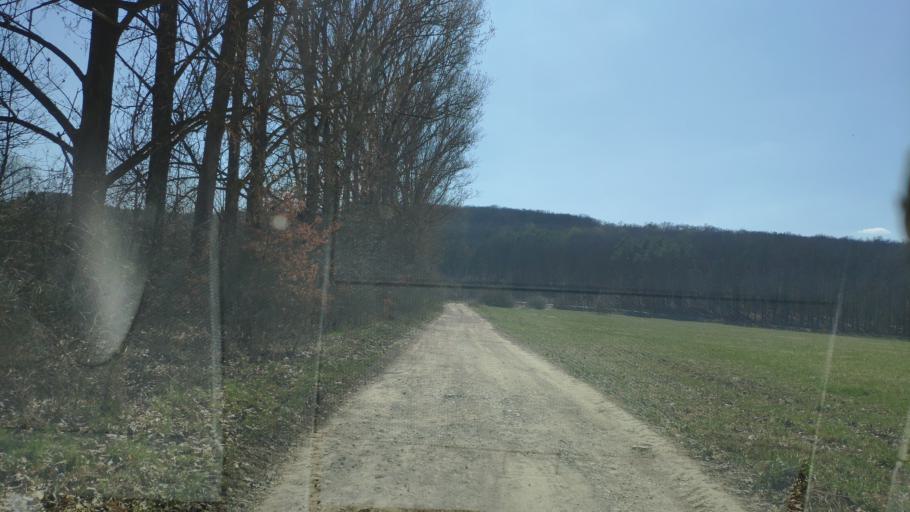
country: SK
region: Kosicky
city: Moldava nad Bodvou
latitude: 48.5680
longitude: 20.9434
